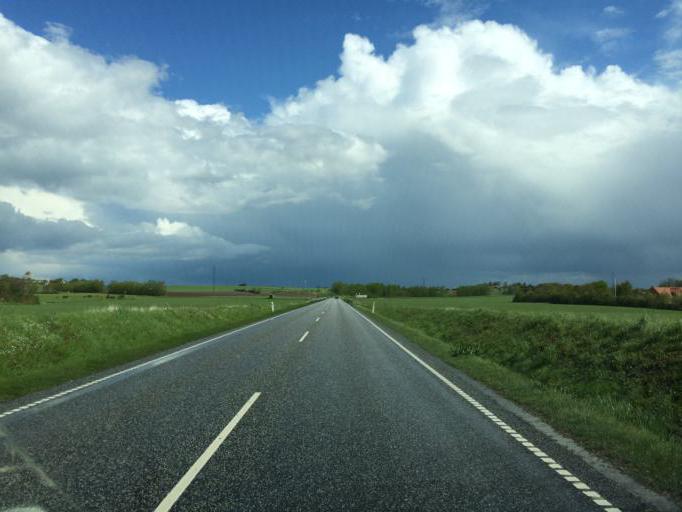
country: DK
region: Central Jutland
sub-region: Holstebro Kommune
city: Vinderup
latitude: 56.4391
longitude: 8.7209
